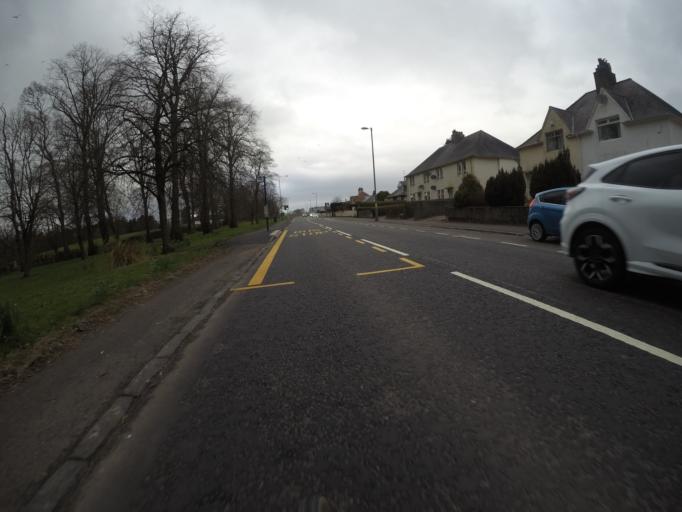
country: GB
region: Scotland
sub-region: East Ayrshire
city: Kilmarnock
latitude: 55.6112
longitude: -4.5203
